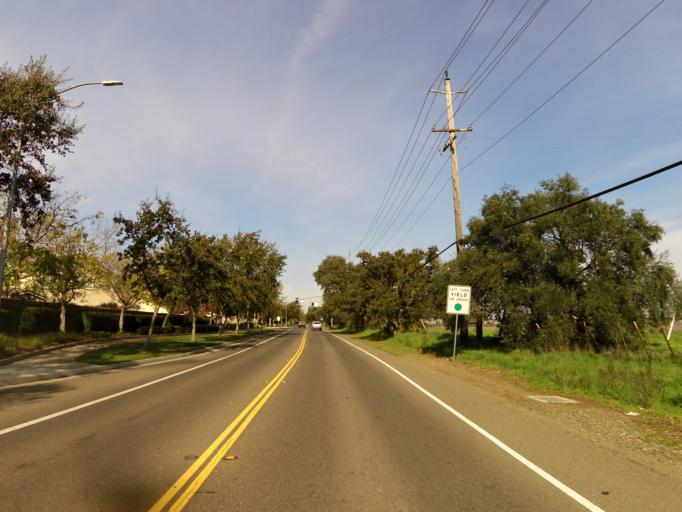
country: US
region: California
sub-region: Sacramento County
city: Laguna
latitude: 38.3856
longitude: -121.4173
